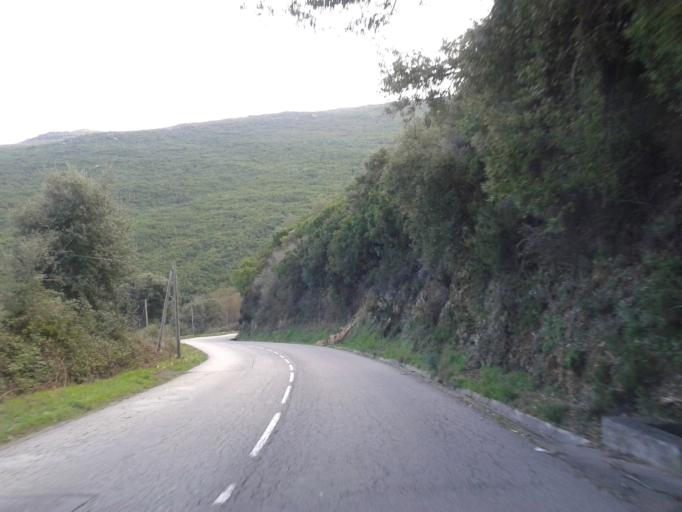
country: FR
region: Corsica
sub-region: Departement de la Haute-Corse
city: Biguglia
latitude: 42.5987
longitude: 9.4103
